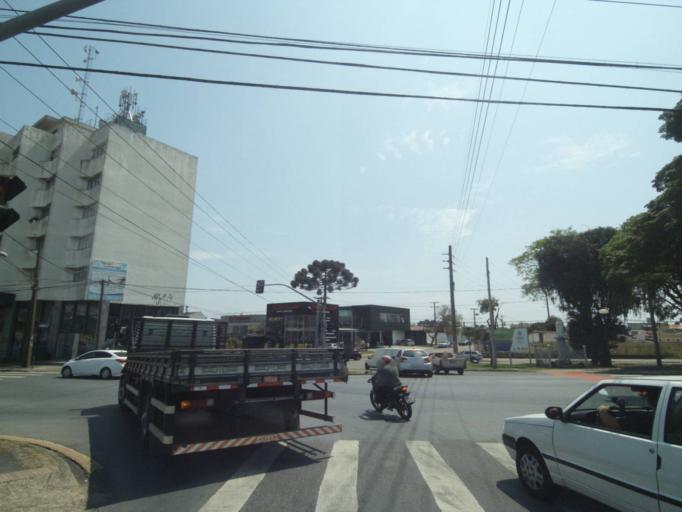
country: BR
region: Parana
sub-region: Curitiba
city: Curitiba
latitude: -25.4781
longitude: -49.3113
